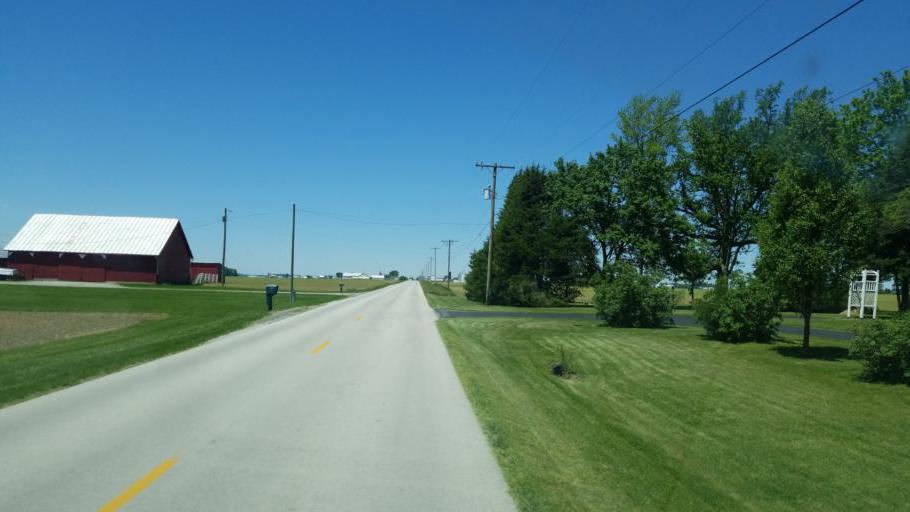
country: US
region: Ohio
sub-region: Auglaize County
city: Minster
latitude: 40.3856
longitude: -84.4151
